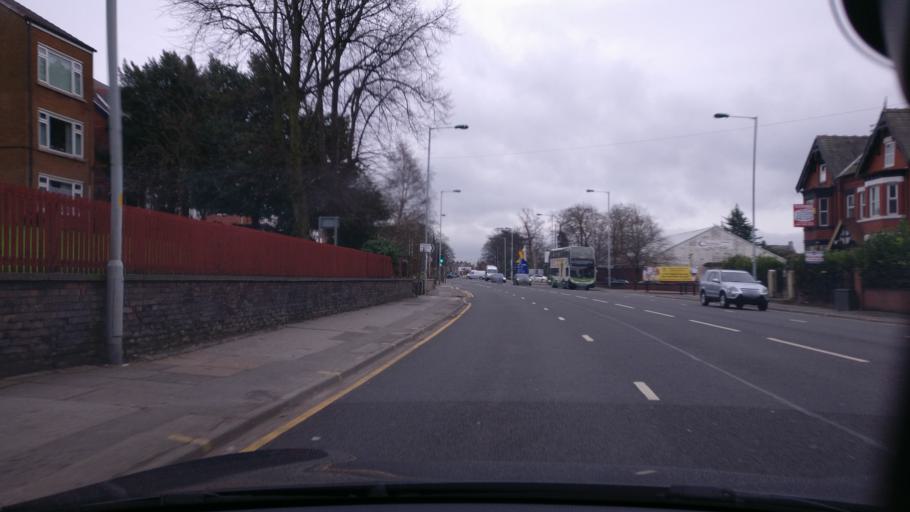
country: GB
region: England
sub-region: Borough of Stockport
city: Stockport
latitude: 53.3918
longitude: -2.1447
